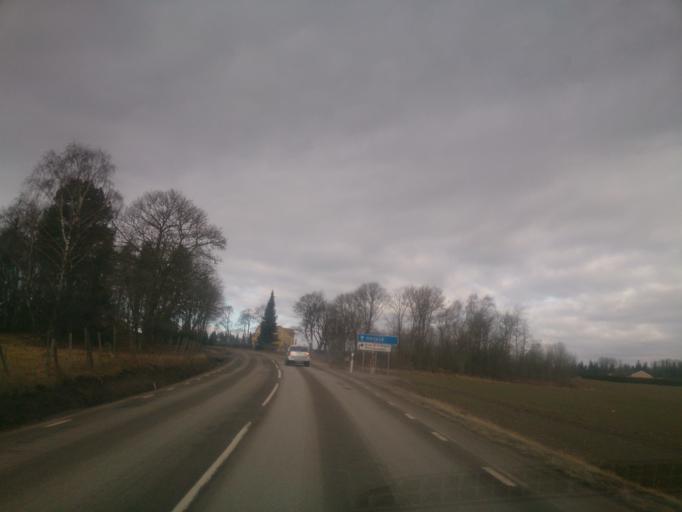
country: SE
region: OEstergoetland
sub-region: Motala Kommun
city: Stenstorp
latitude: 58.5198
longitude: 15.0800
